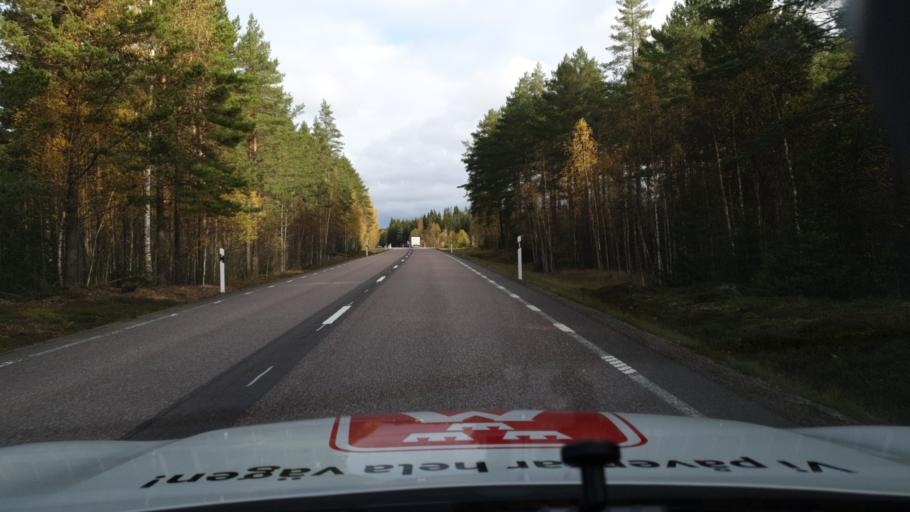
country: SE
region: Gaevleborg
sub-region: Gavle Kommun
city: Hedesunda
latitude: 60.3520
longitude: 16.9607
